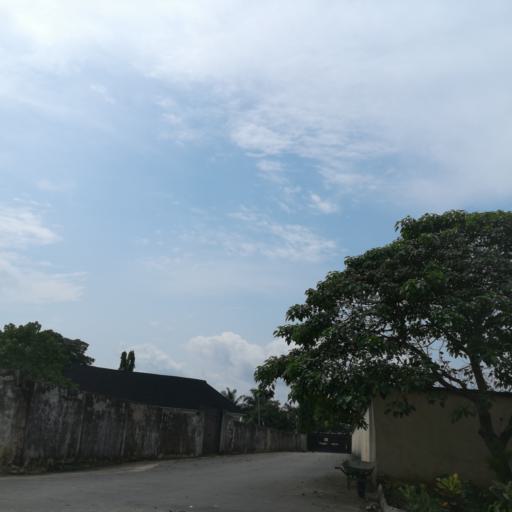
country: NG
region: Rivers
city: Port Harcourt
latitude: 4.8400
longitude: 7.0145
